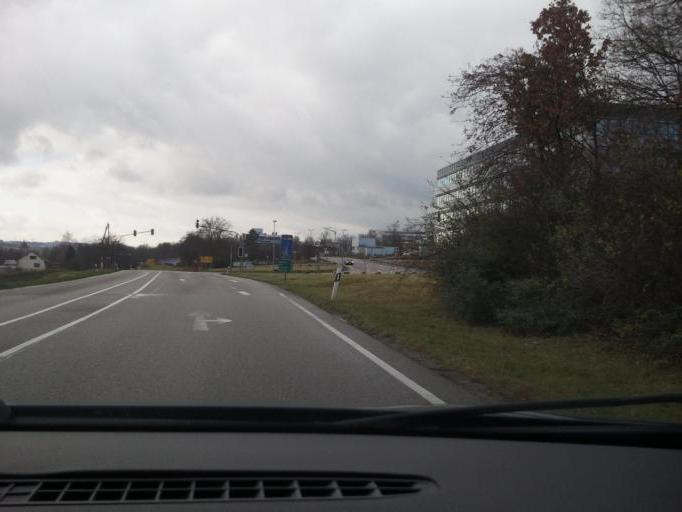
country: DE
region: Baden-Wuerttemberg
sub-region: Regierungsbezirk Stuttgart
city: Schwieberdingen
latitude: 48.8808
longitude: 9.0855
